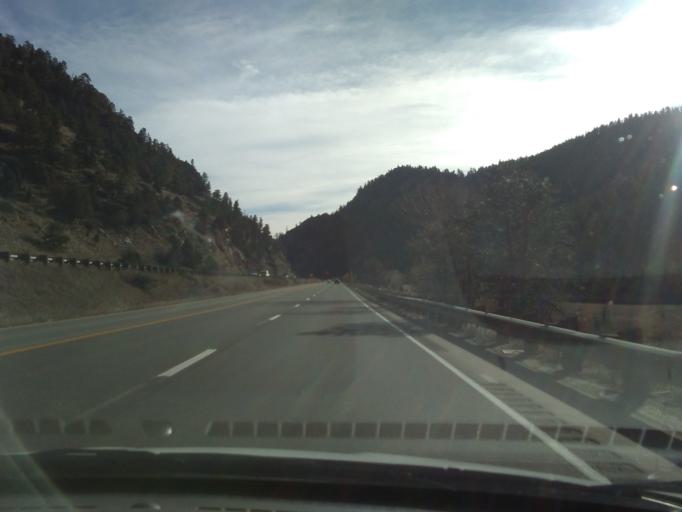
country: US
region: Colorado
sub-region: Clear Creek County
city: Idaho Springs
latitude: 39.7583
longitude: -105.5690
